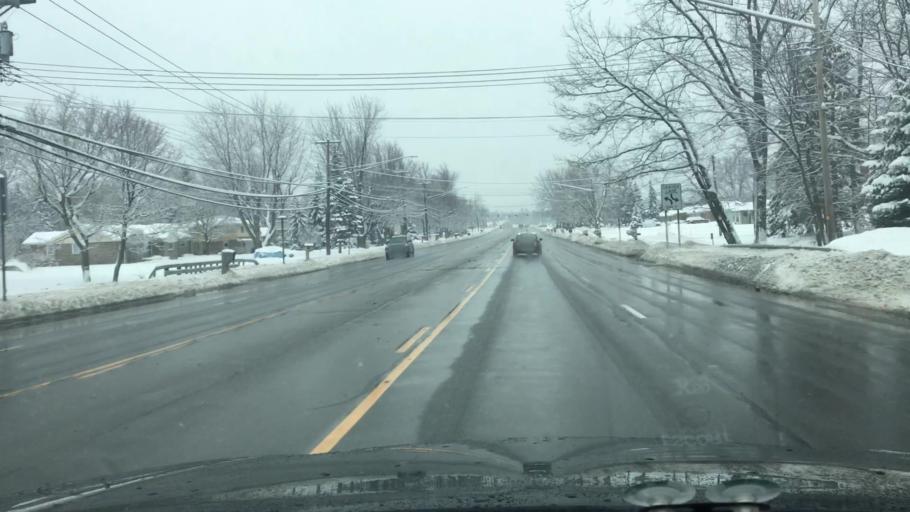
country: US
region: New York
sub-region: Erie County
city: Orchard Park
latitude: 42.8068
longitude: -78.7519
